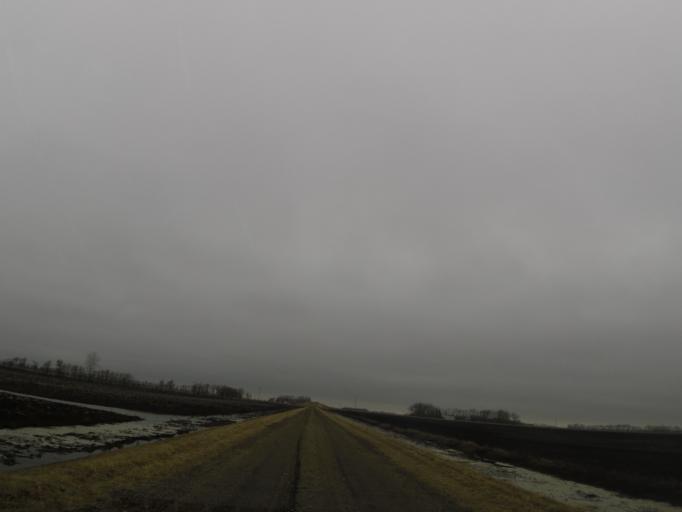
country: US
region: North Dakota
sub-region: Walsh County
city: Grafton
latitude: 48.3831
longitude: -97.1808
